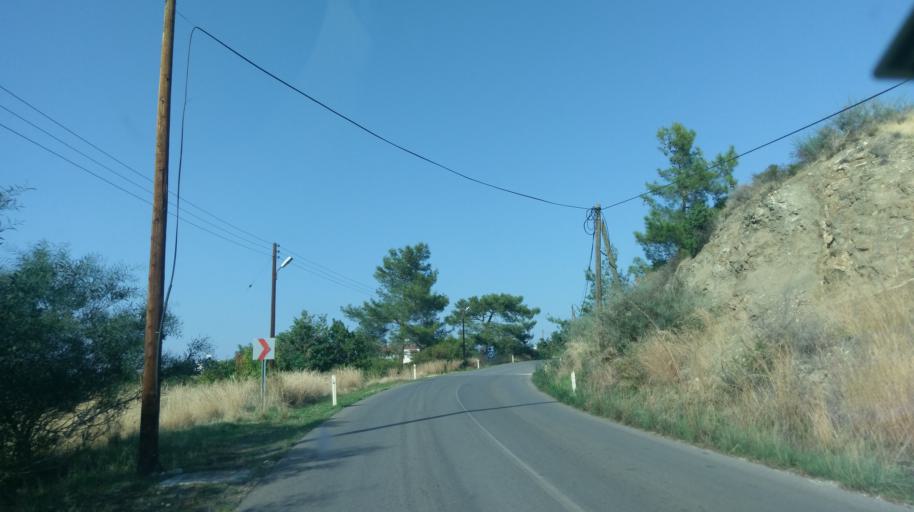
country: CY
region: Lefkosia
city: Kato Pyrgos
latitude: 35.1573
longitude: 32.7613
